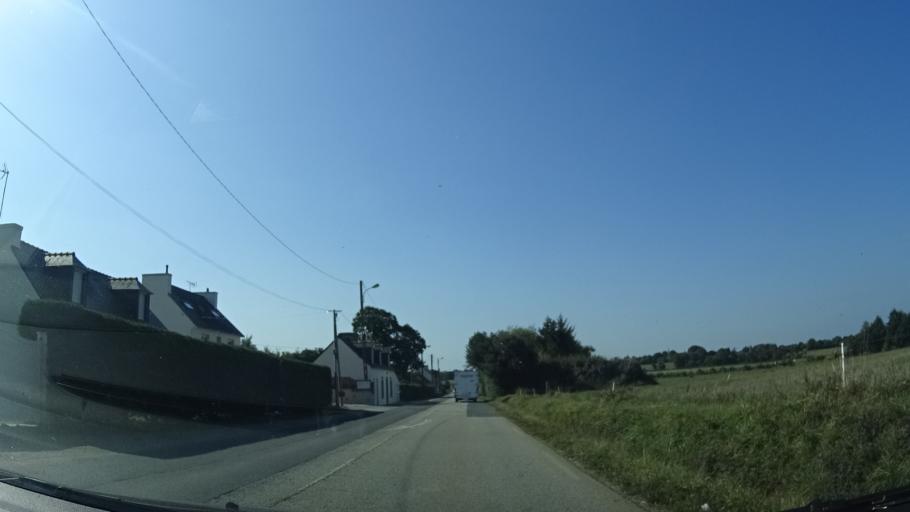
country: FR
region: Brittany
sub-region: Departement du Finistere
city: Cast
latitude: 48.1525
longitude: -4.1421
